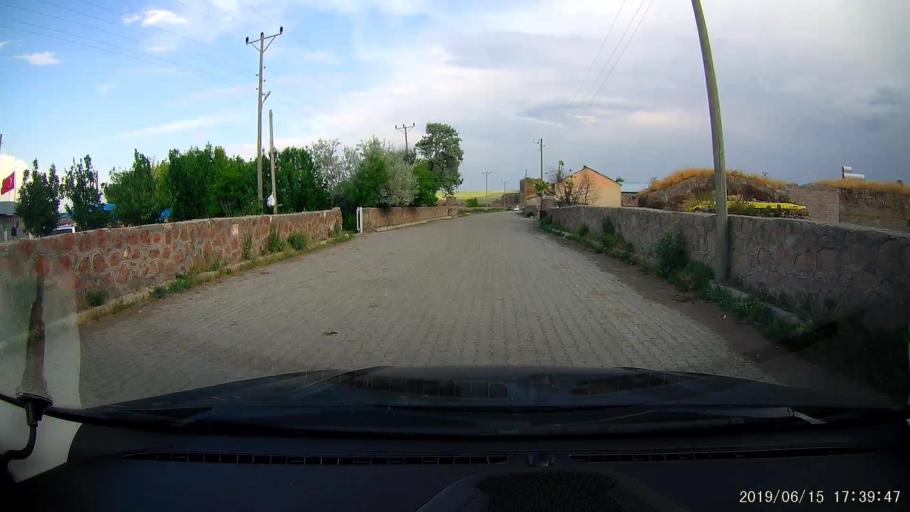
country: TR
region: Kars
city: Basgedikler
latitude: 40.5145
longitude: 43.5711
